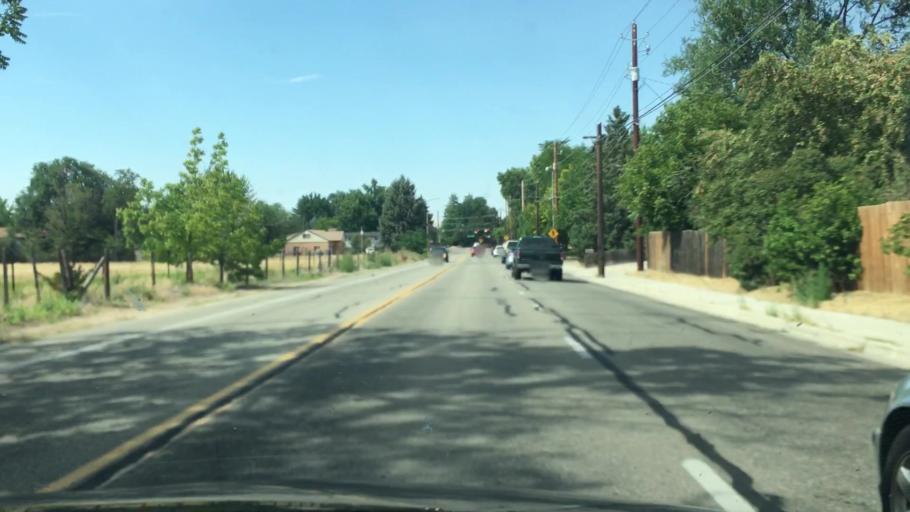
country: US
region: Idaho
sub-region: Ada County
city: Garden City
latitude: 43.6398
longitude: -116.2743
